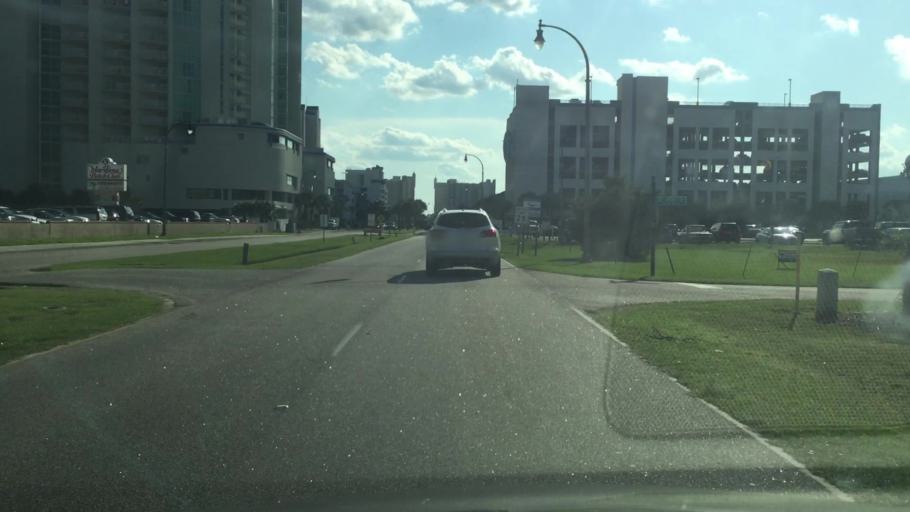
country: US
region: South Carolina
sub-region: Horry County
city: North Myrtle Beach
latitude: 33.8211
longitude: -78.6663
